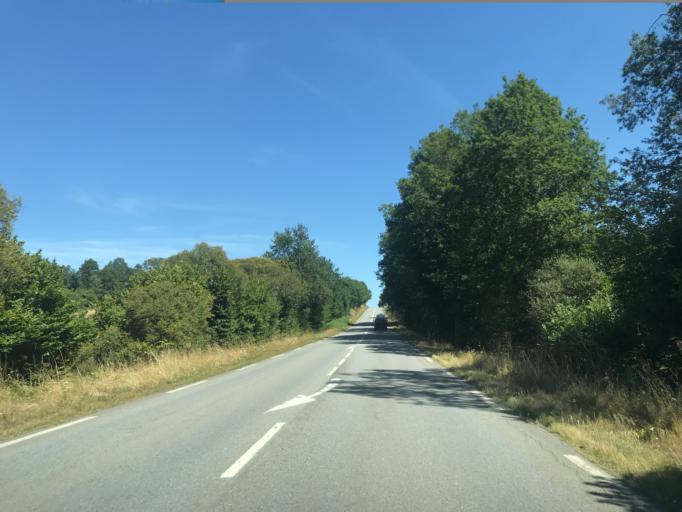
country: FR
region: Limousin
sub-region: Departement de la Correze
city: Meymac
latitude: 45.4901
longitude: 2.2046
